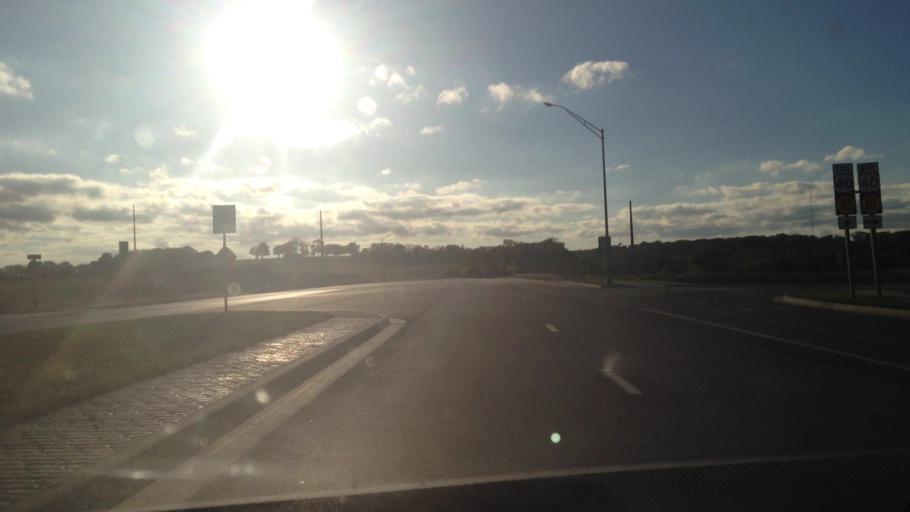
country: US
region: Kansas
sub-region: Douglas County
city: Lawrence
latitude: 38.9602
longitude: -95.3327
